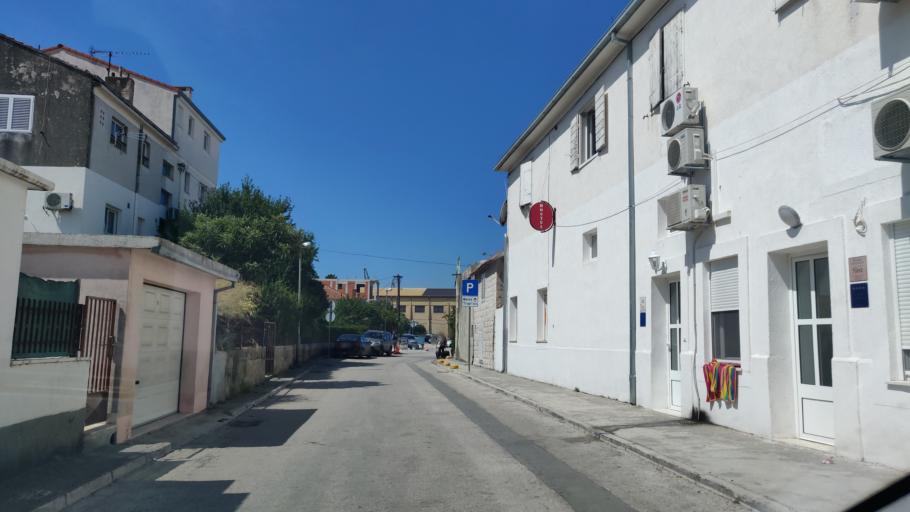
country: HR
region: Splitsko-Dalmatinska
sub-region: Grad Trogir
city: Trogir
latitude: 43.5132
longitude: 16.2486
